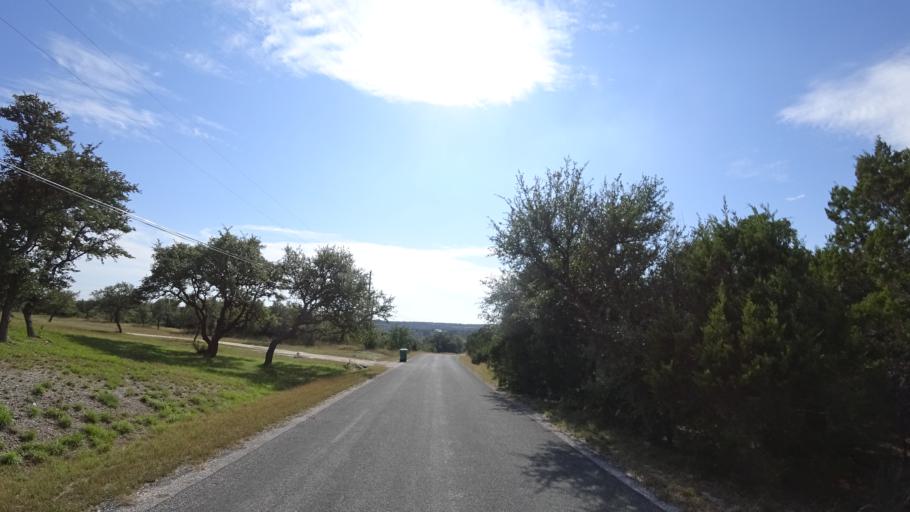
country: US
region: Texas
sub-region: Travis County
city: Bee Cave
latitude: 30.2203
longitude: -97.9365
